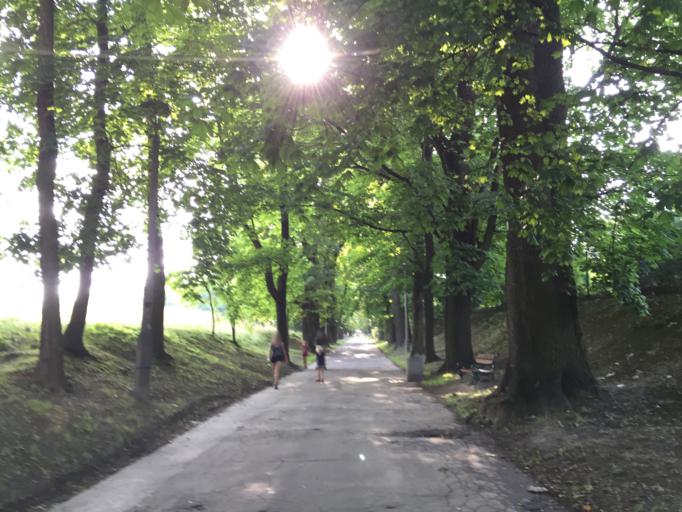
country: PL
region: Lesser Poland Voivodeship
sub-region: Krakow
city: Krakow
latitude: 50.0533
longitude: 19.9034
